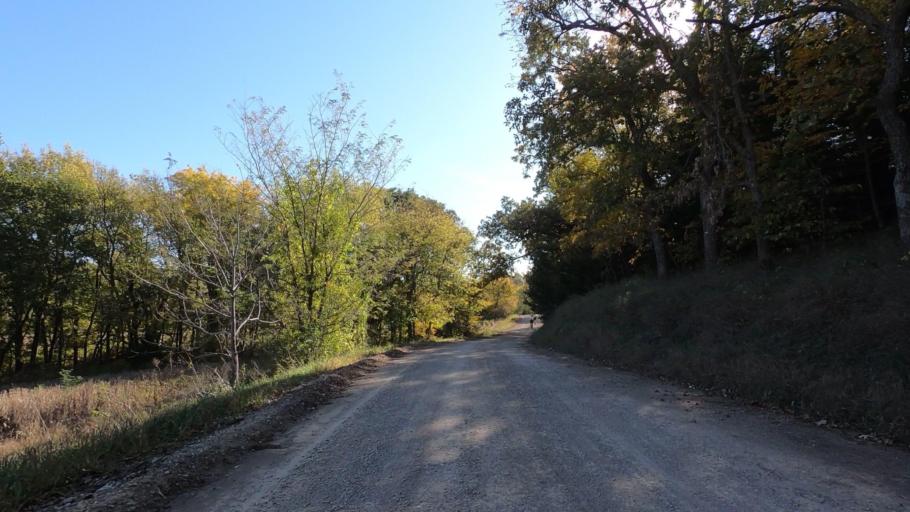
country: US
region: Kansas
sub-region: Marshall County
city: Blue Rapids
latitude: 39.4895
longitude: -96.6098
